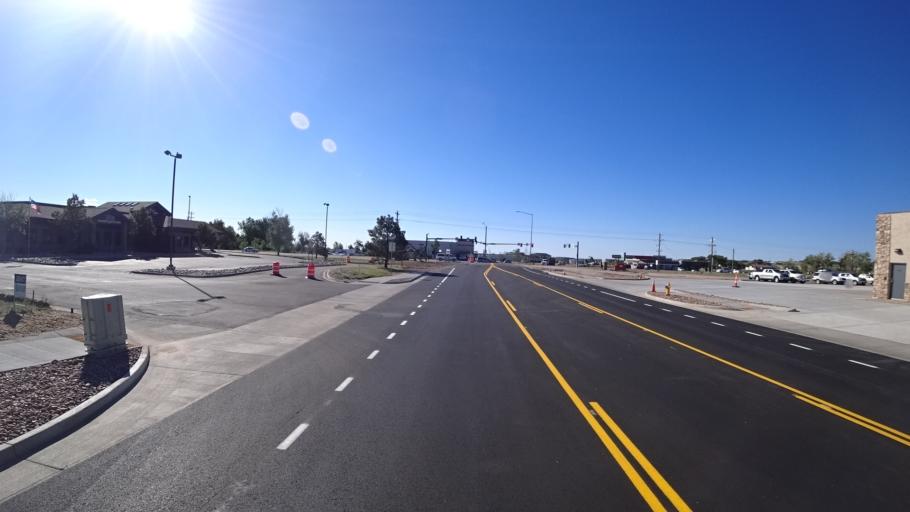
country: US
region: Colorado
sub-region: El Paso County
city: Cimarron Hills
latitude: 38.9341
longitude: -104.6093
